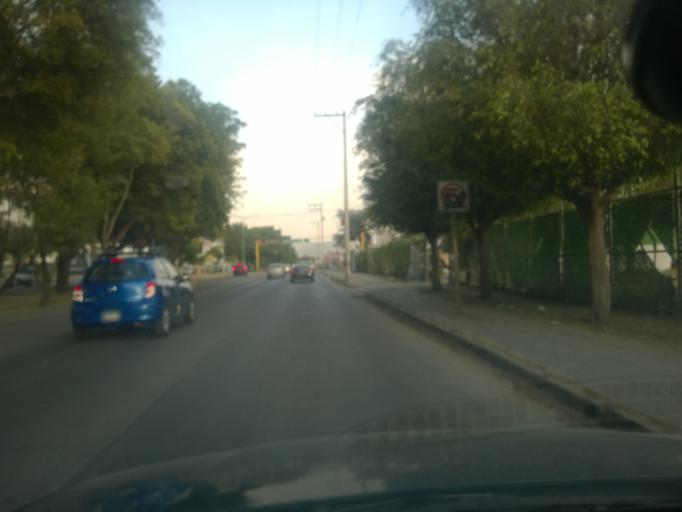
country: MX
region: Guanajuato
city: Leon
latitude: 21.1473
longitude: -101.6817
